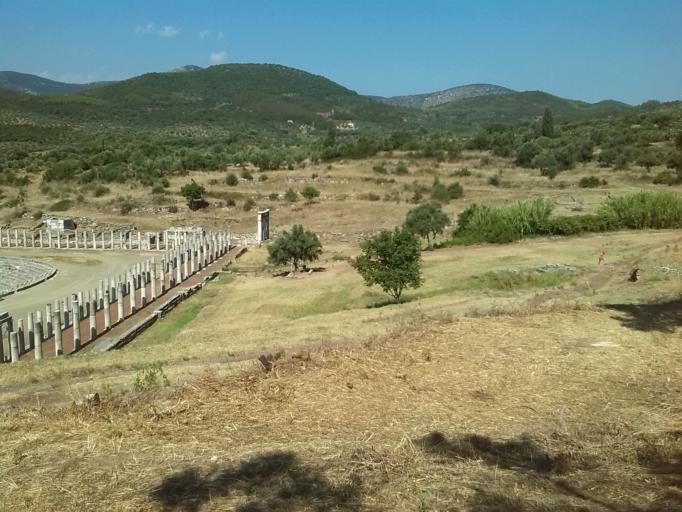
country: GR
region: Peloponnese
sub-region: Nomos Messinias
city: Meligalas
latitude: 37.1737
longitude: 21.9204
